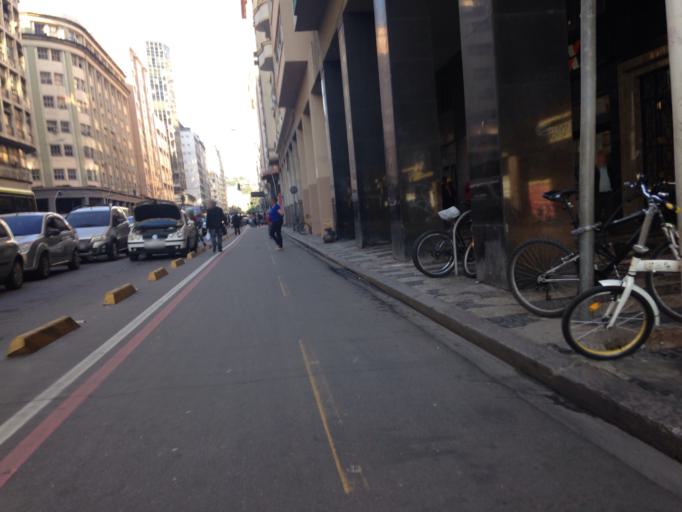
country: BR
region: Rio de Janeiro
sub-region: Niteroi
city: Niteroi
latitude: -22.8935
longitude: -43.1230
